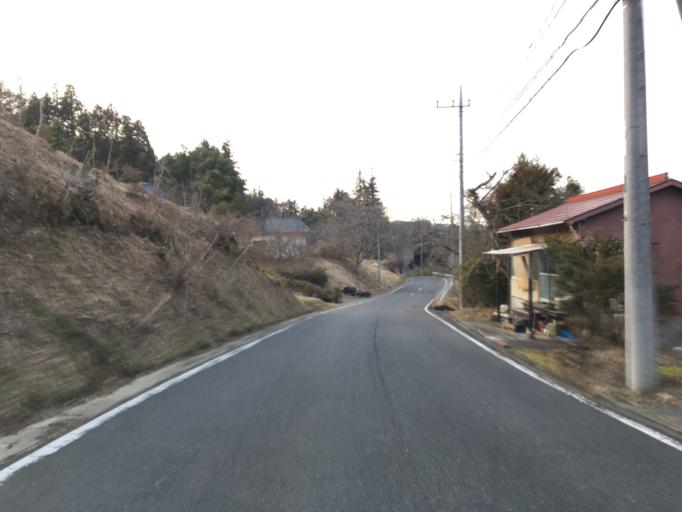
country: JP
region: Ibaraki
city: Daigo
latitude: 36.8002
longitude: 140.3929
